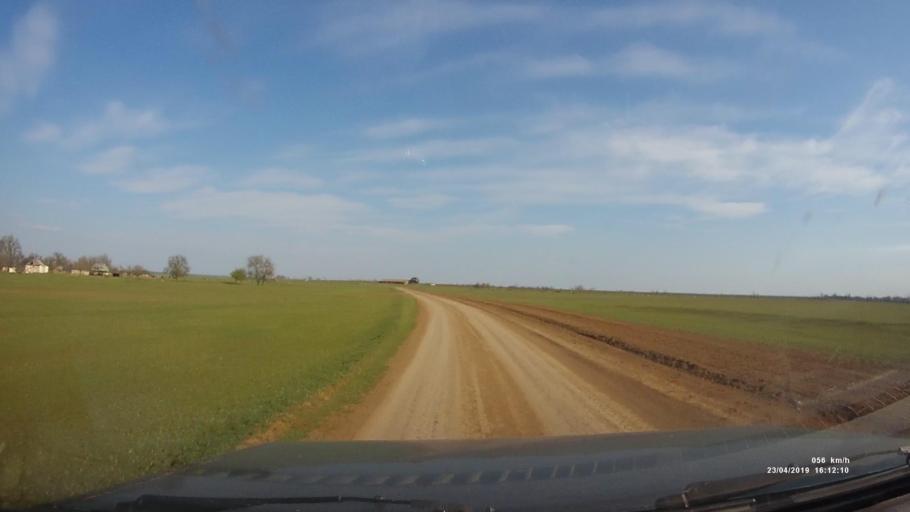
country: RU
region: Kalmykiya
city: Priyutnoye
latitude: 46.4679
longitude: 43.1238
